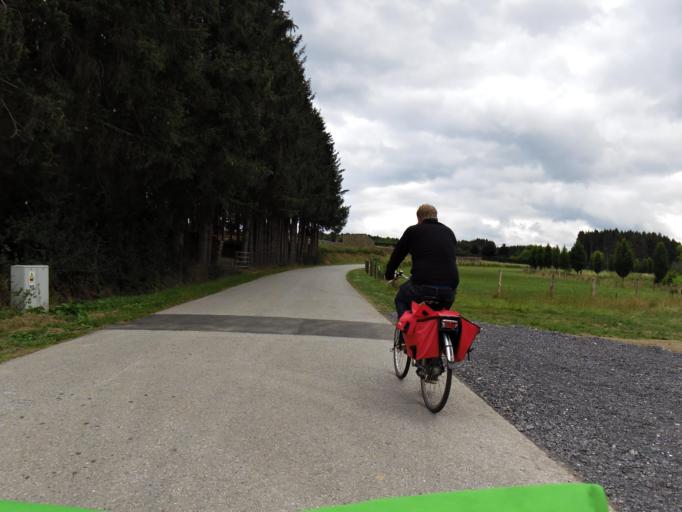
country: BE
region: Wallonia
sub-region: Province de Namur
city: Bievre
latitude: 49.9368
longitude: 5.0181
